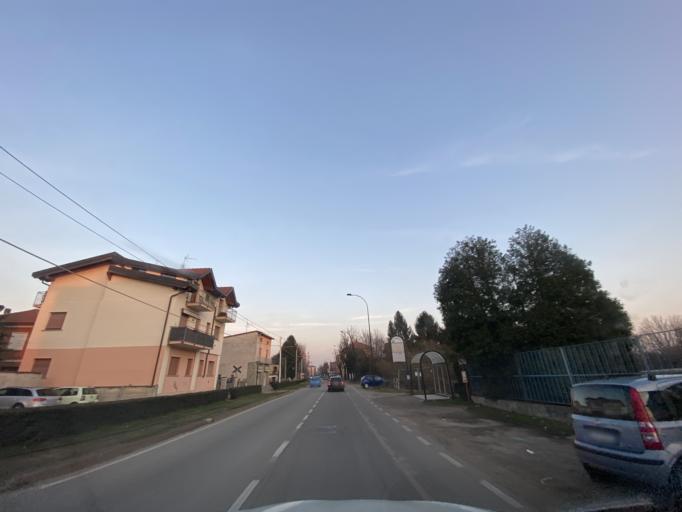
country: IT
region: Lombardy
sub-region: Provincia di Monza e Brianza
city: Limbiate
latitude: 45.5987
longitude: 9.1351
